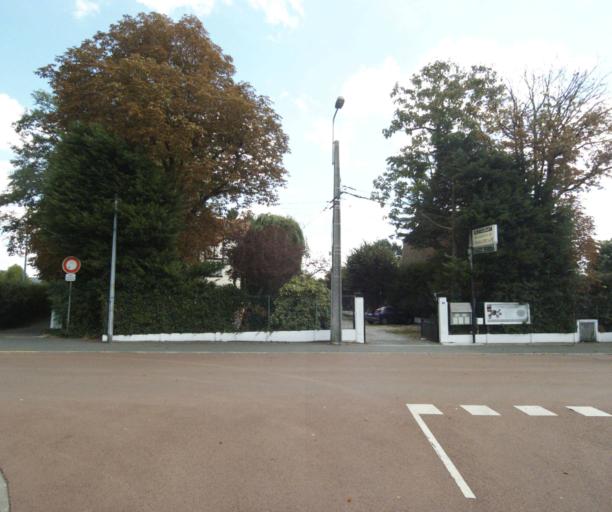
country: FR
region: Nord-Pas-de-Calais
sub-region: Departement du Nord
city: Mons-en-Baroeul
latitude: 50.6386
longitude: 3.1172
